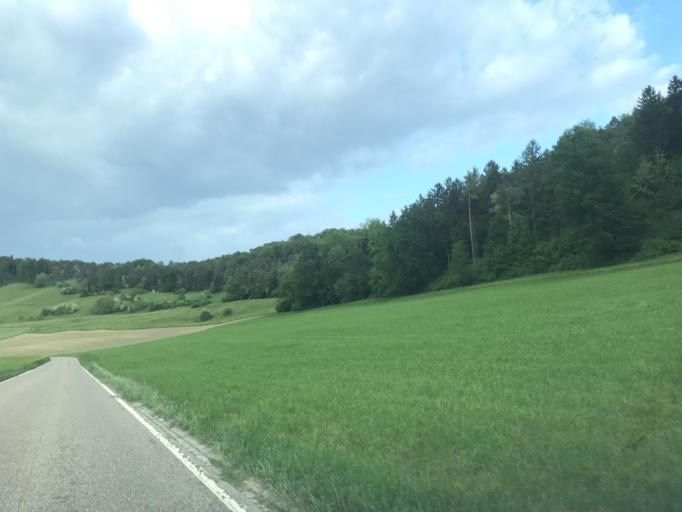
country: CH
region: Zurich
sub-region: Bezirk Winterthur
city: Wuelflingen (Kreis 6) / Oberfeld
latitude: 47.4911
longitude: 8.6871
